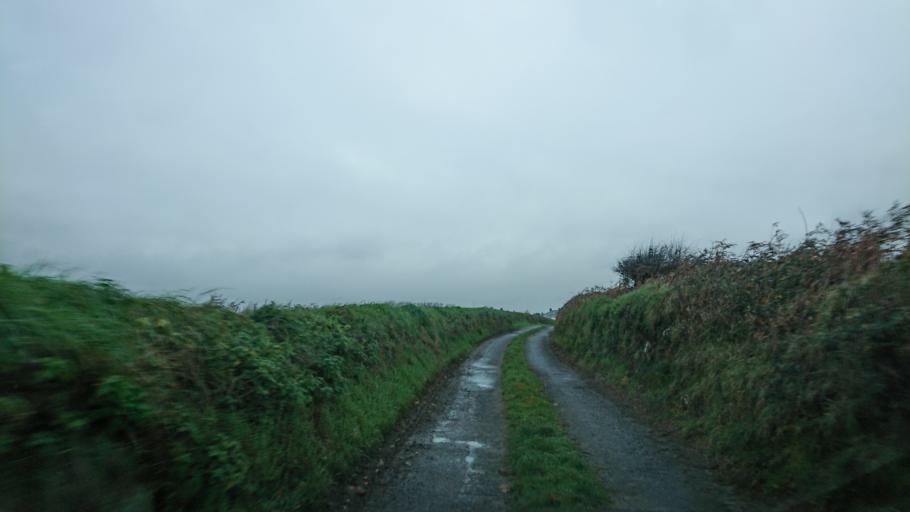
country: IE
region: Munster
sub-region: Waterford
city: Tra Mhor
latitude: 52.1966
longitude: -7.1373
